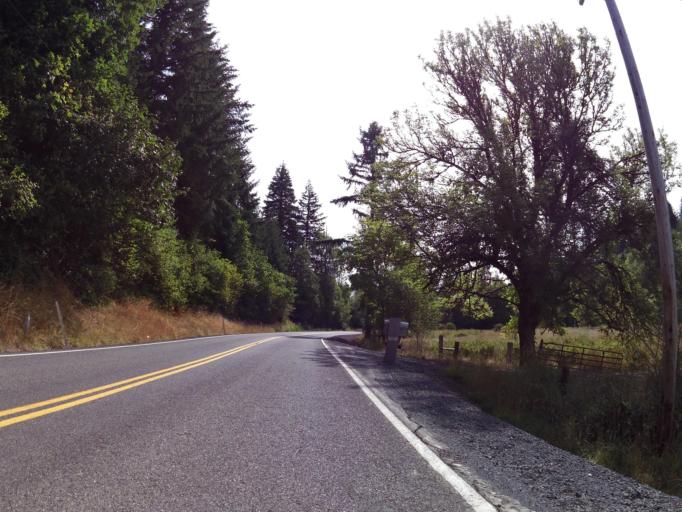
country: US
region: Washington
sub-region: Lewis County
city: Napavine
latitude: 46.5674
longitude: -122.9667
